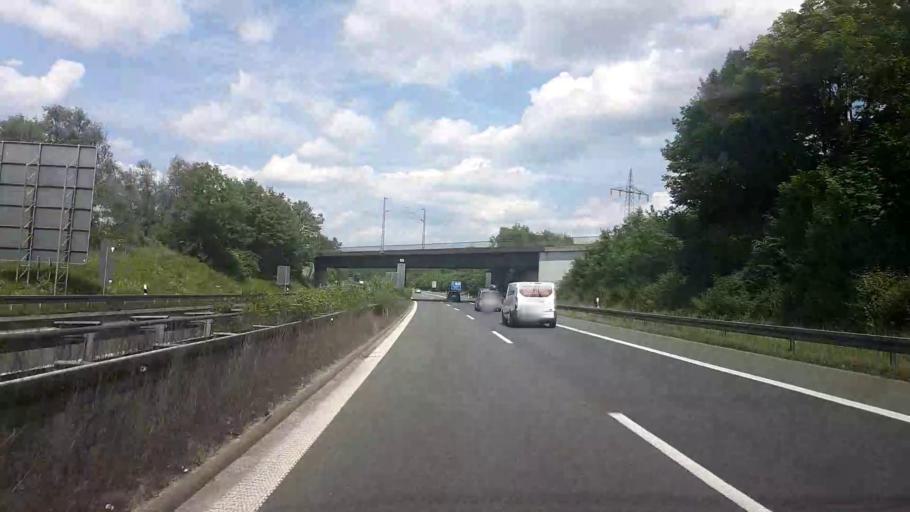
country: DE
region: Bavaria
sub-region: Upper Franconia
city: Eggolsheim
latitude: 49.7457
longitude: 11.0585
